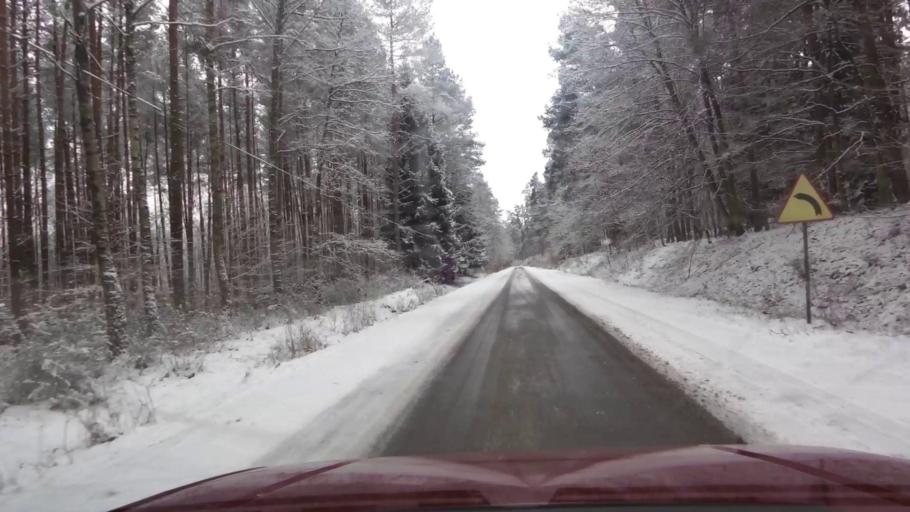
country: PL
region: West Pomeranian Voivodeship
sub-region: Powiat swidwinski
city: Rabino
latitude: 53.8956
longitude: 15.9399
